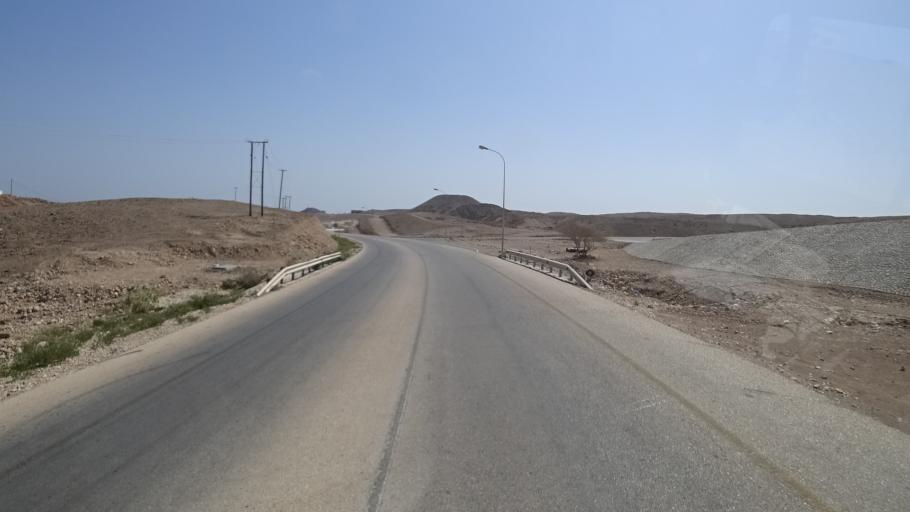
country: OM
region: Ash Sharqiyah
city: Sur
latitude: 22.5454
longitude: 59.5196
